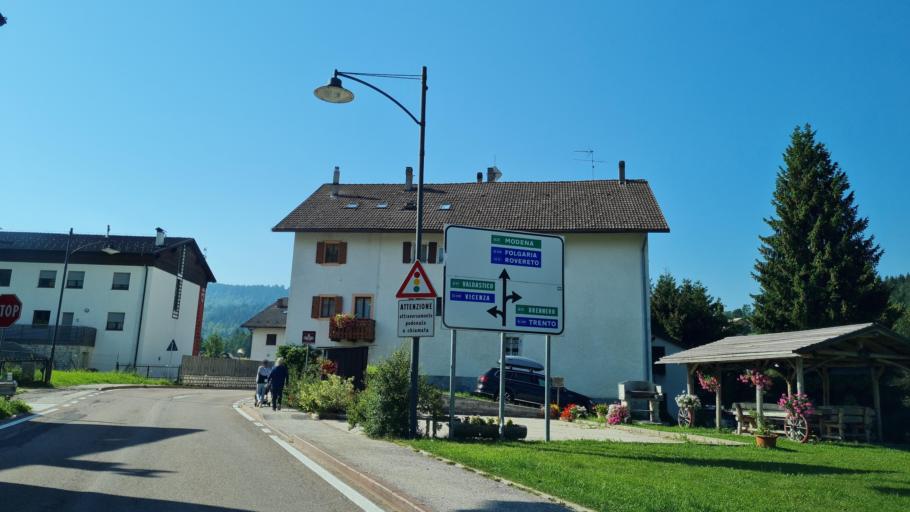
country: IT
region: Trentino-Alto Adige
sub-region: Provincia di Trento
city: Centa San Nicolo
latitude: 45.9364
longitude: 11.2269
